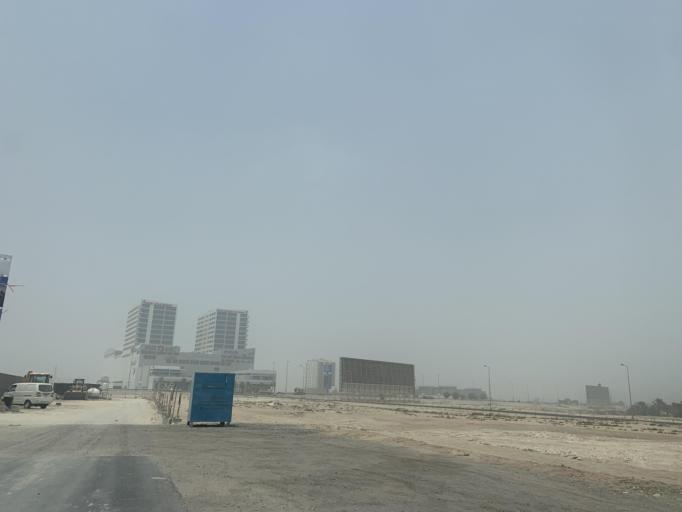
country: BH
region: Central Governorate
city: Madinat Hamad
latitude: 26.1723
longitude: 50.4834
